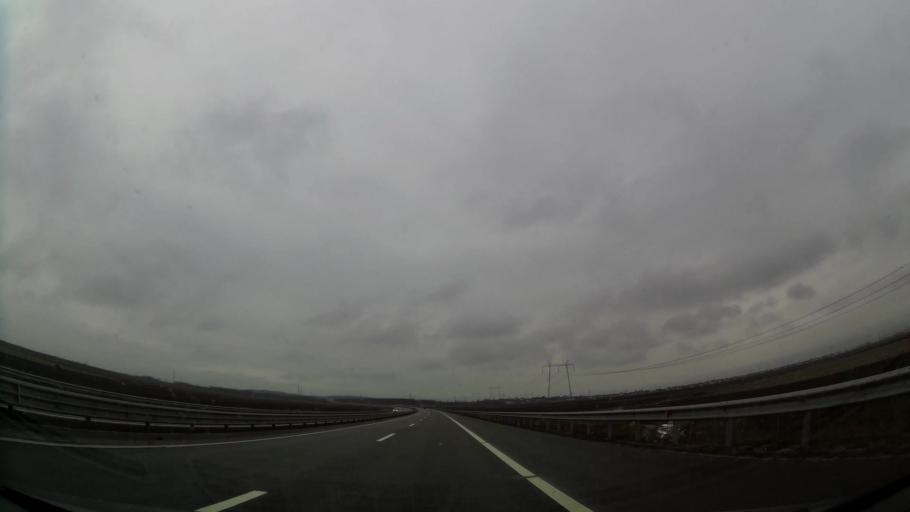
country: XK
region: Ferizaj
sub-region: Komuna e Ferizajt
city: Ferizaj
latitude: 42.3903
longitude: 21.1997
